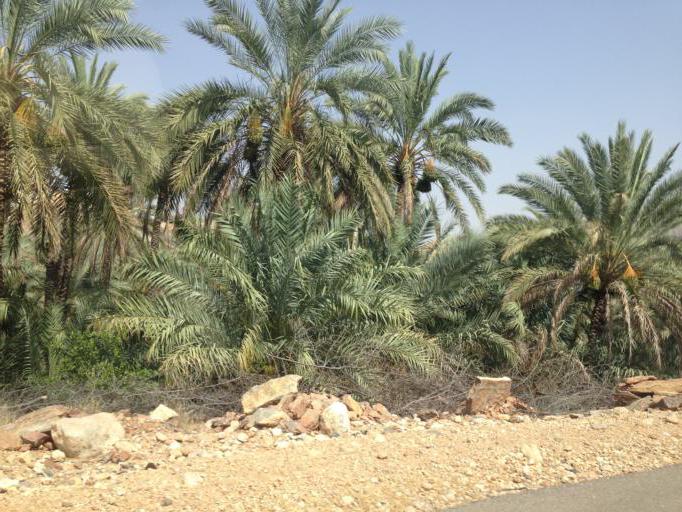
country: OM
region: Ash Sharqiyah
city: Ibra'
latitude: 23.0830
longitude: 58.8658
